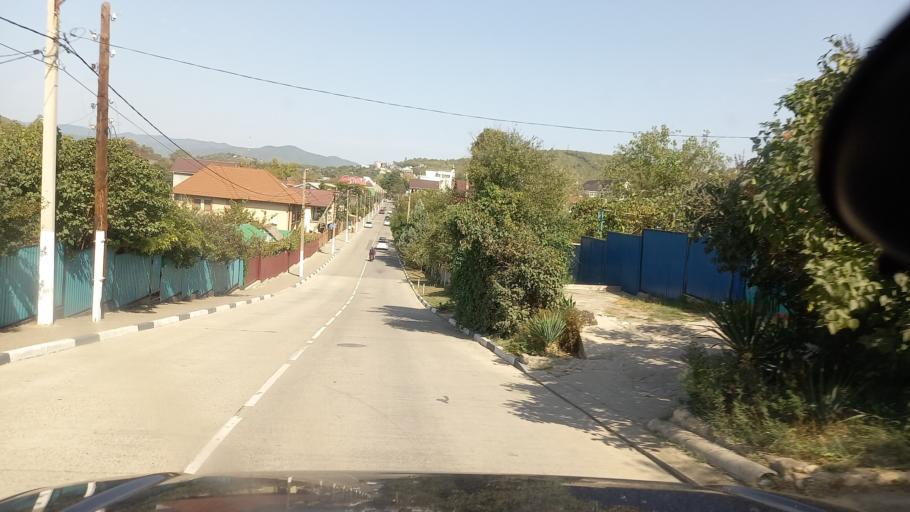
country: RU
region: Krasnodarskiy
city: Arkhipo-Osipovka
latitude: 44.3666
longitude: 38.5315
